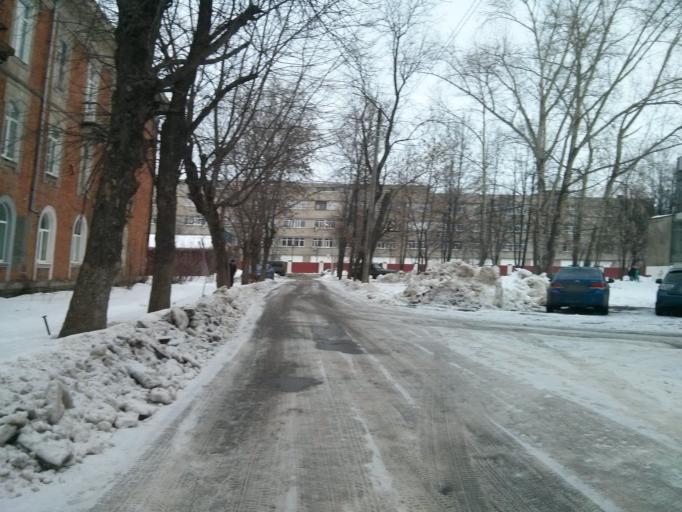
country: RU
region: Vladimir
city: Murom
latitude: 55.5547
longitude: 42.0598
